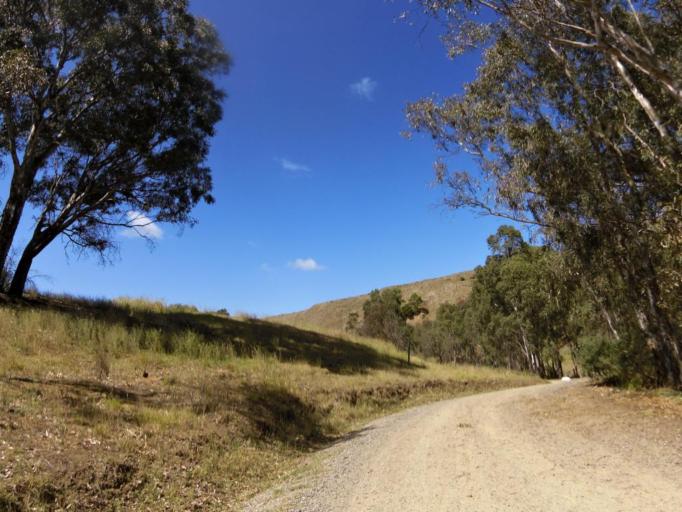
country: AU
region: Victoria
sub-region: Brimbank
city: Kealba
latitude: -37.7403
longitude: 144.8333
